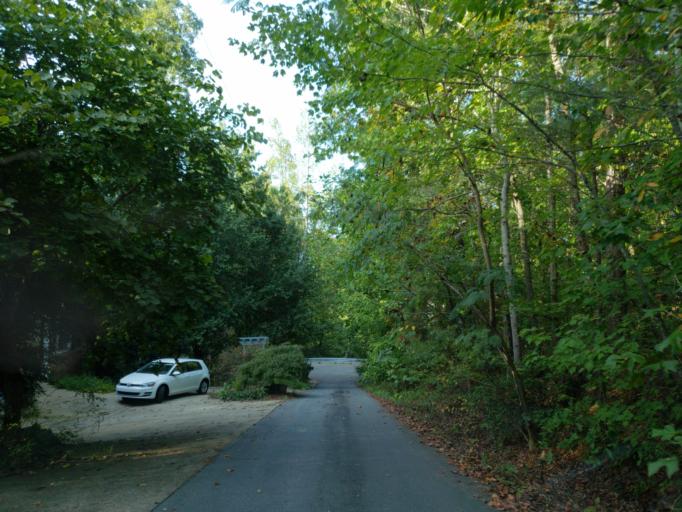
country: US
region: Georgia
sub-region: Fulton County
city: Roswell
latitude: 34.0825
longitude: -84.4060
